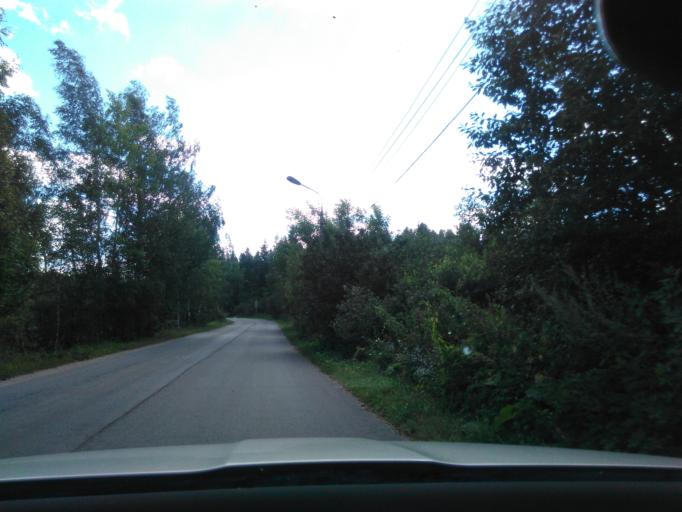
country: RU
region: Moskovskaya
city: Klin
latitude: 56.2359
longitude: 36.8335
